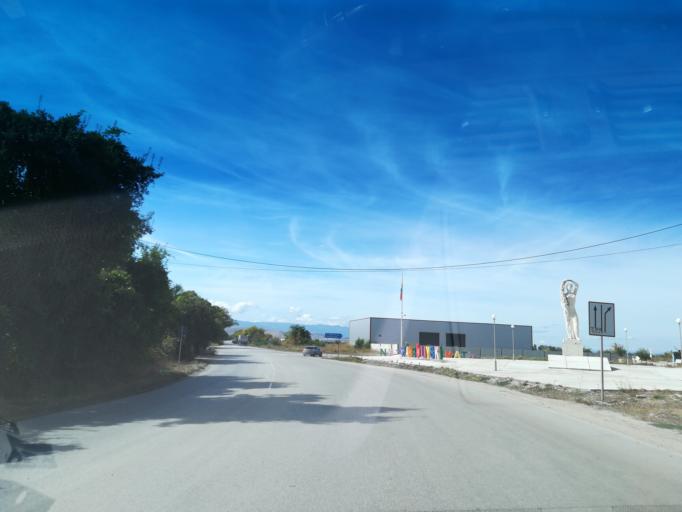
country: BG
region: Plovdiv
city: Stamboliyski
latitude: 42.1201
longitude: 24.5535
